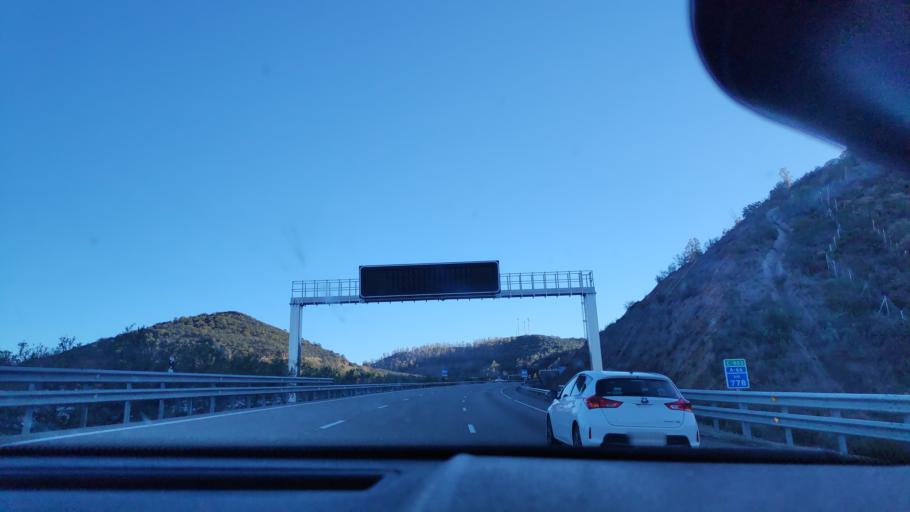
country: ES
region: Andalusia
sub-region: Provincia de Sevilla
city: El Ronquillo
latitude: 37.6604
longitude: -6.1653
